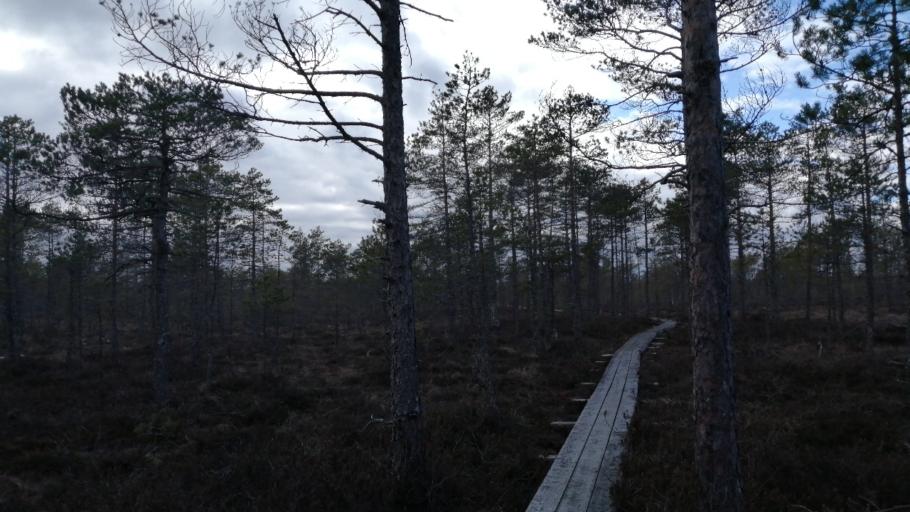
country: EE
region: Ida-Virumaa
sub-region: Kohtla-Nomme vald
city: Kohtla-Nomme
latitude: 59.1705
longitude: 27.2754
